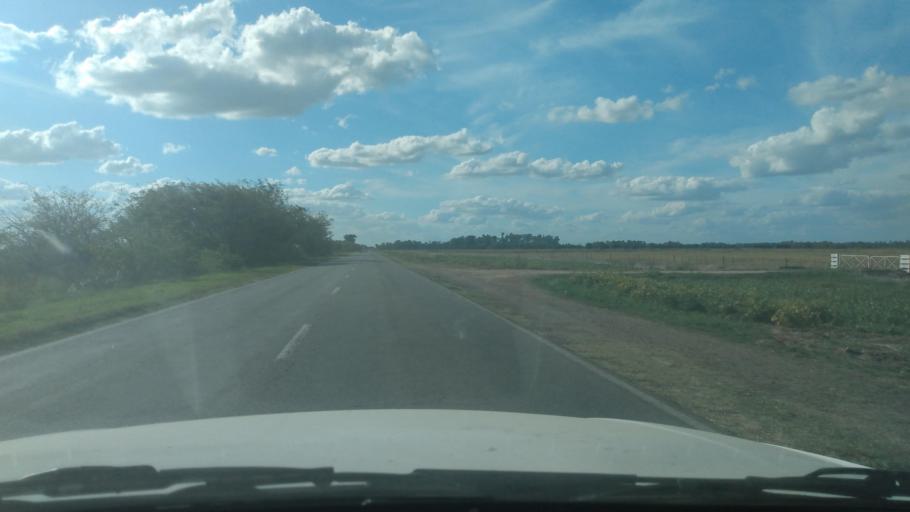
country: AR
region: Buenos Aires
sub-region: Partido de Navarro
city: Navarro
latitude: -34.9707
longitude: -59.3174
